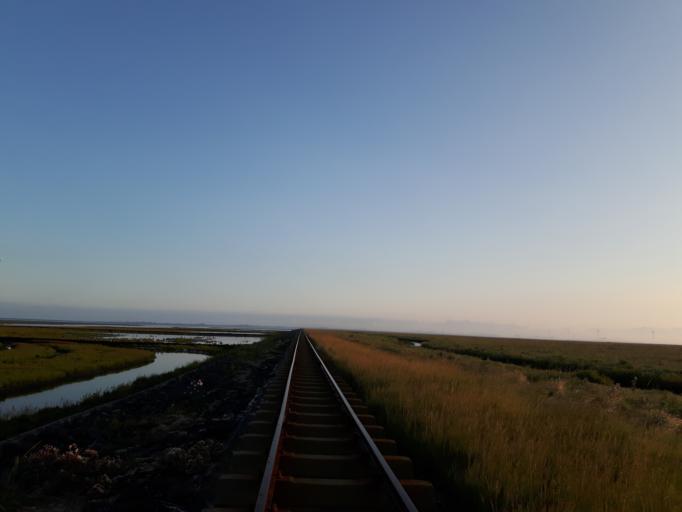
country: DE
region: Schleswig-Holstein
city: Dagebull
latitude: 54.6884
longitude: 8.7102
